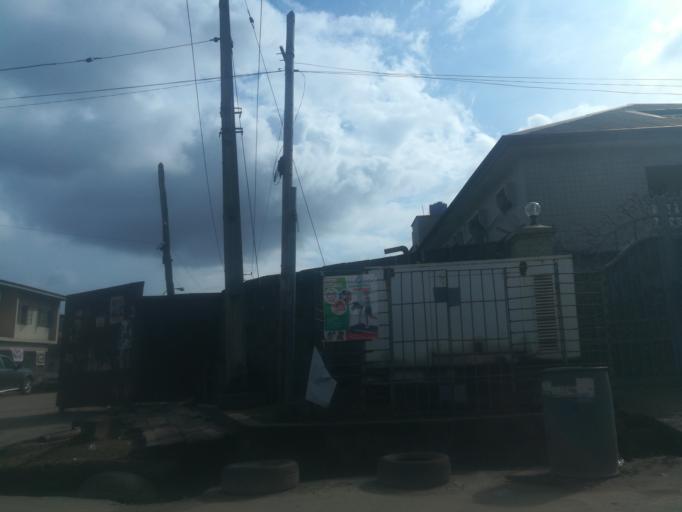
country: NG
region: Lagos
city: Somolu
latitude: 6.5488
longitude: 3.3752
